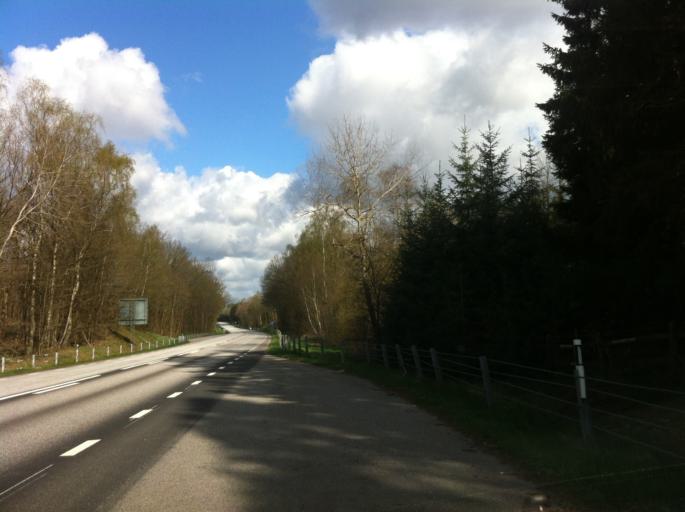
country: SE
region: Skane
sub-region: Hoors Kommun
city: Satofta
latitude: 55.9067
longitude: 13.6073
